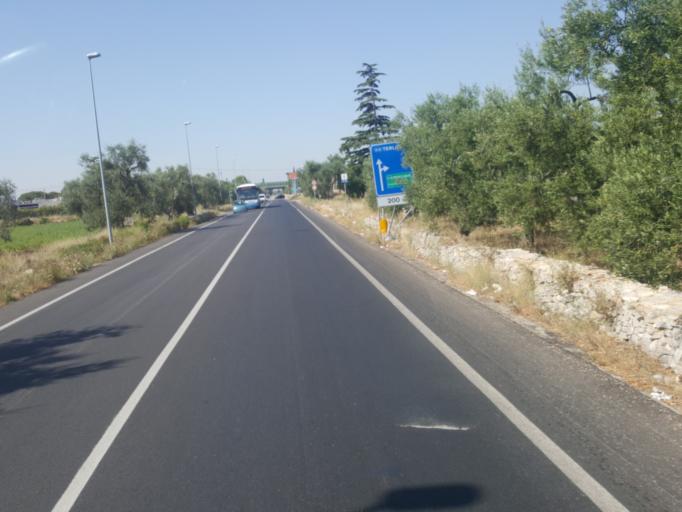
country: IT
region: Apulia
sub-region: Provincia di Bari
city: Molfetta
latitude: 41.1790
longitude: 16.5799
